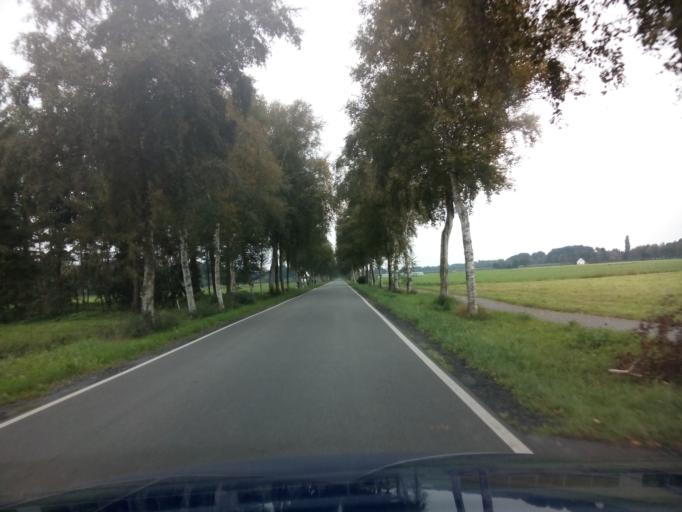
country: DE
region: Lower Saxony
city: Grasberg
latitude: 53.2459
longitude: 8.9961
